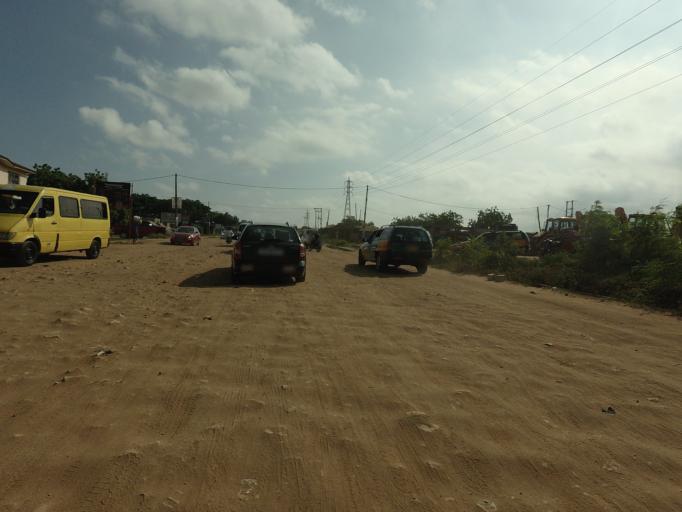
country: GH
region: Greater Accra
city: Tema
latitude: 5.6743
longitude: -0.0432
